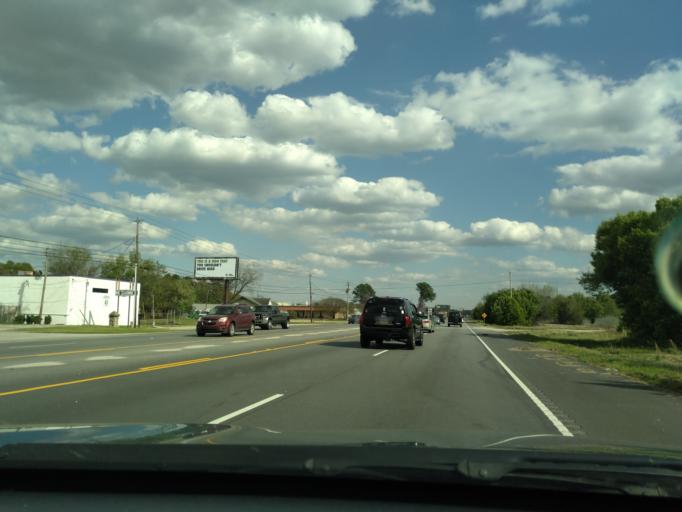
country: US
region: South Carolina
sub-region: Florence County
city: Florence
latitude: 34.2158
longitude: -79.7821
